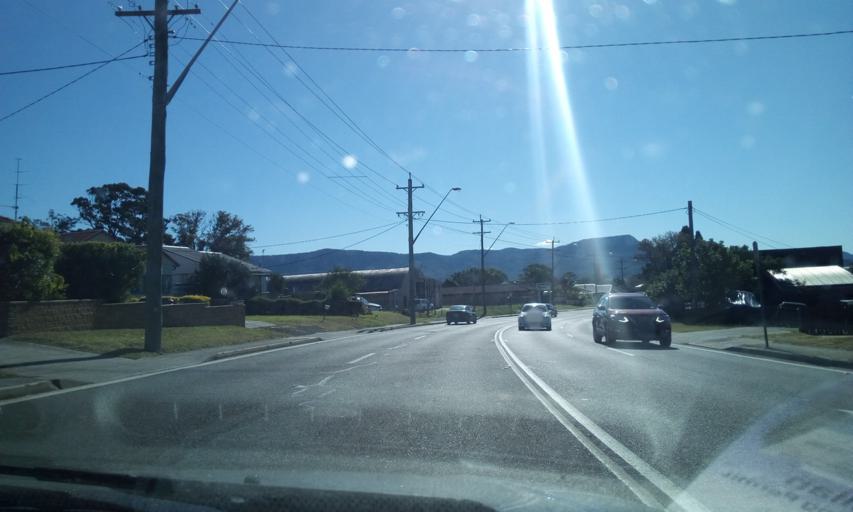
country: AU
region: New South Wales
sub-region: Wollongong
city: Dapto
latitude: -34.5078
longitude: 150.7859
